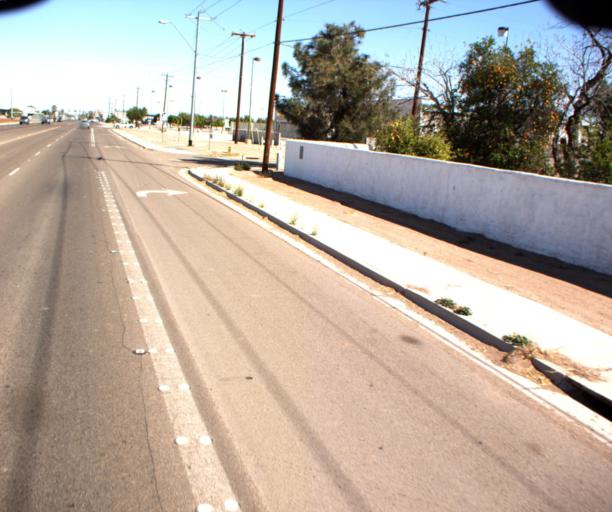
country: US
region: Arizona
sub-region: Yuma County
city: Yuma
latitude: 32.6655
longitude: -114.6501
